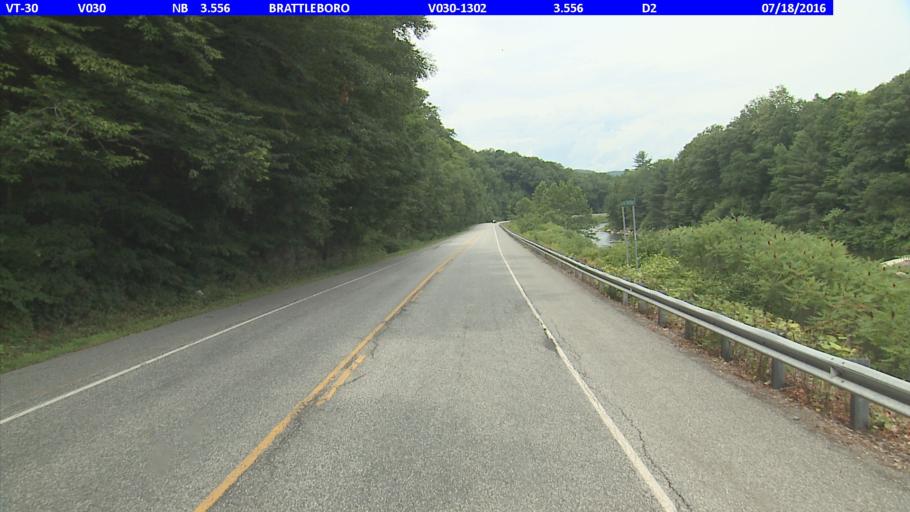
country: US
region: Vermont
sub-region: Windham County
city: West Brattleboro
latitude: 42.8975
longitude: -72.5982
